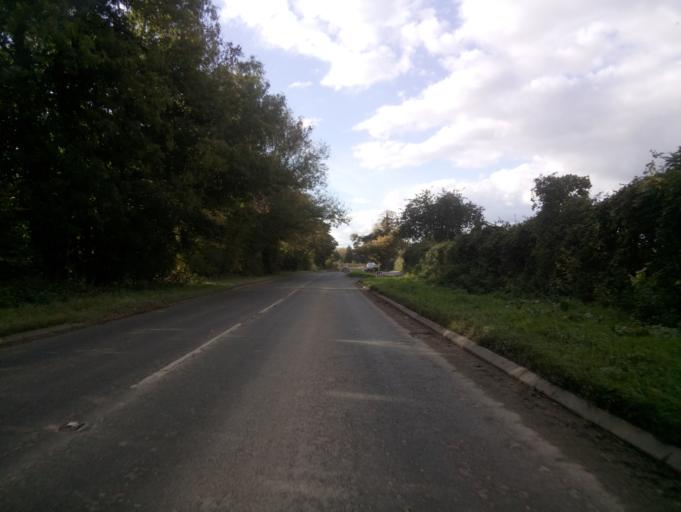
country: GB
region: England
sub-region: Herefordshire
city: Kinnersley
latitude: 52.1167
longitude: -2.9789
